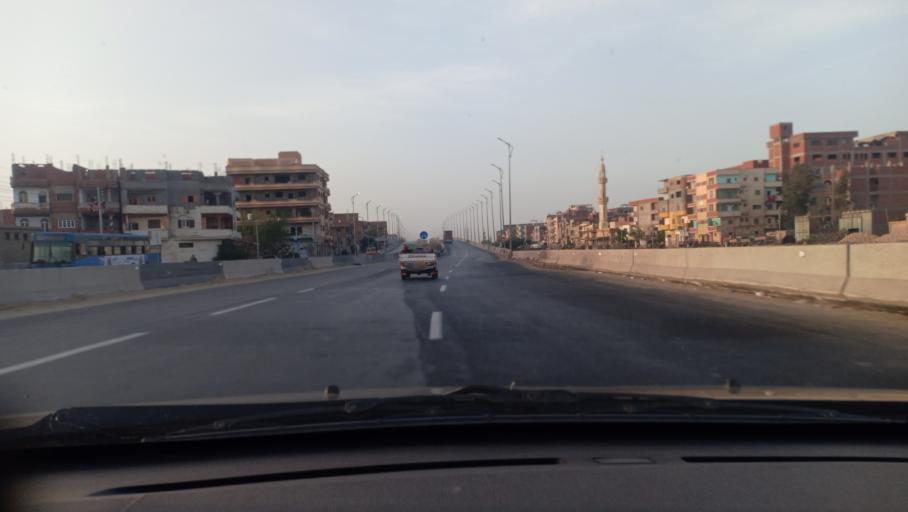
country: EG
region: Muhafazat al Gharbiyah
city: Zifta
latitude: 30.6336
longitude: 31.2800
